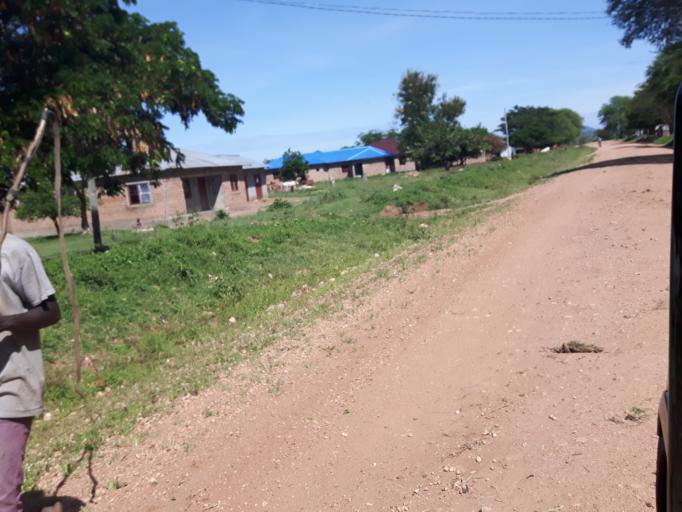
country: TZ
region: Mara
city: Issenye
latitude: -1.9612
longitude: 34.2715
